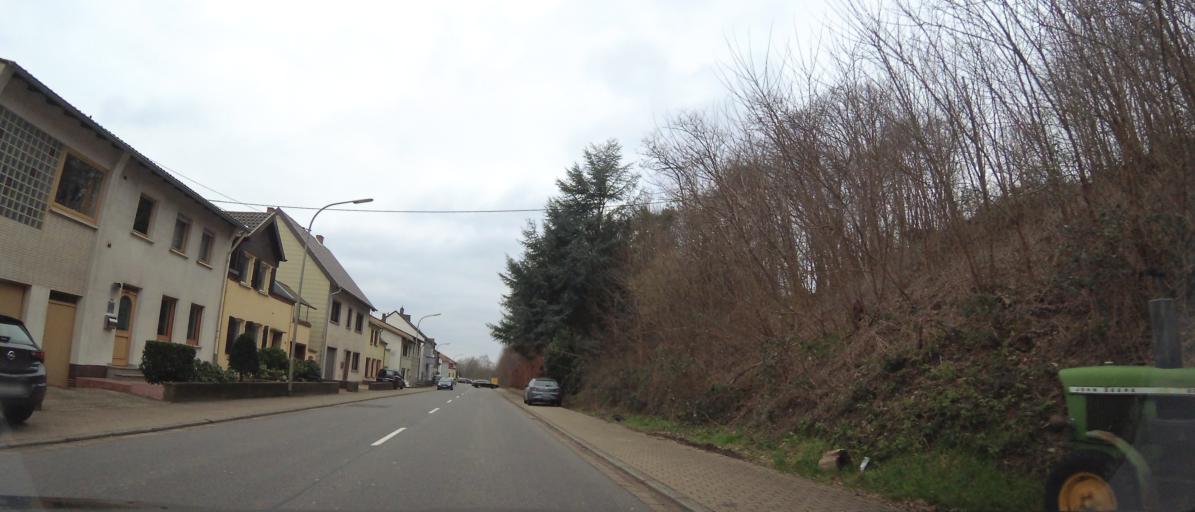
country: DE
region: Saarland
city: Schwalbach
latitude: 49.2890
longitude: 6.8238
